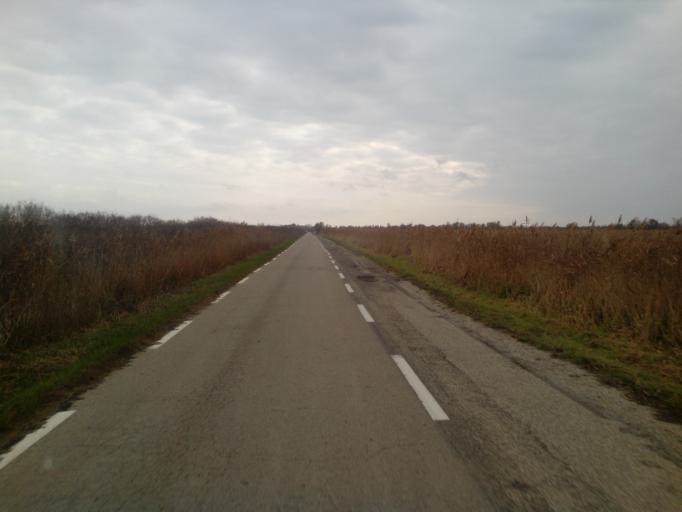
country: FR
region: Languedoc-Roussillon
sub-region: Departement du Gard
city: Vauvert
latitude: 43.6141
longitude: 4.3267
